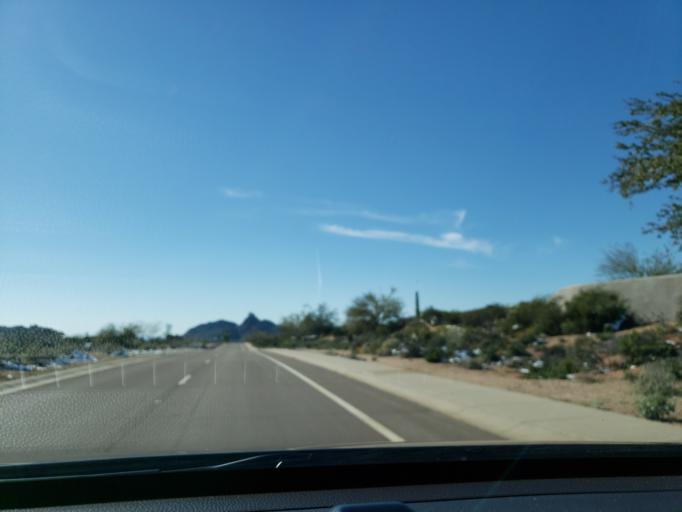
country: US
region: Arizona
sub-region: Maricopa County
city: Carefree
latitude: 33.7269
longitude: -111.8279
